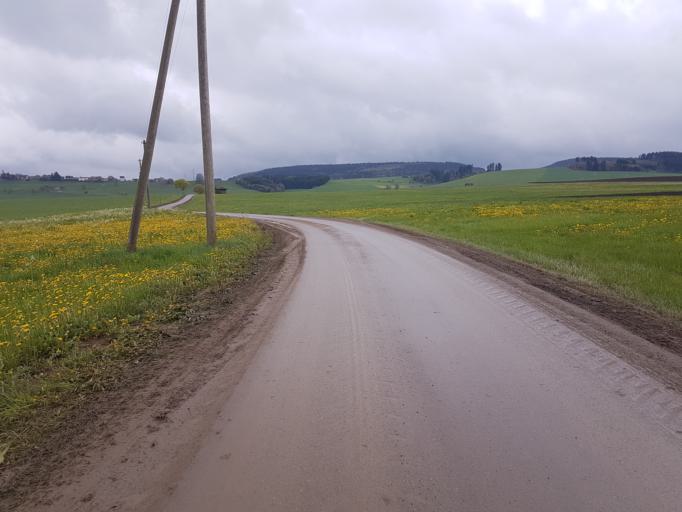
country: DE
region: Baden-Wuerttemberg
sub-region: Freiburg Region
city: Hufingen
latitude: 47.9041
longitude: 8.5382
